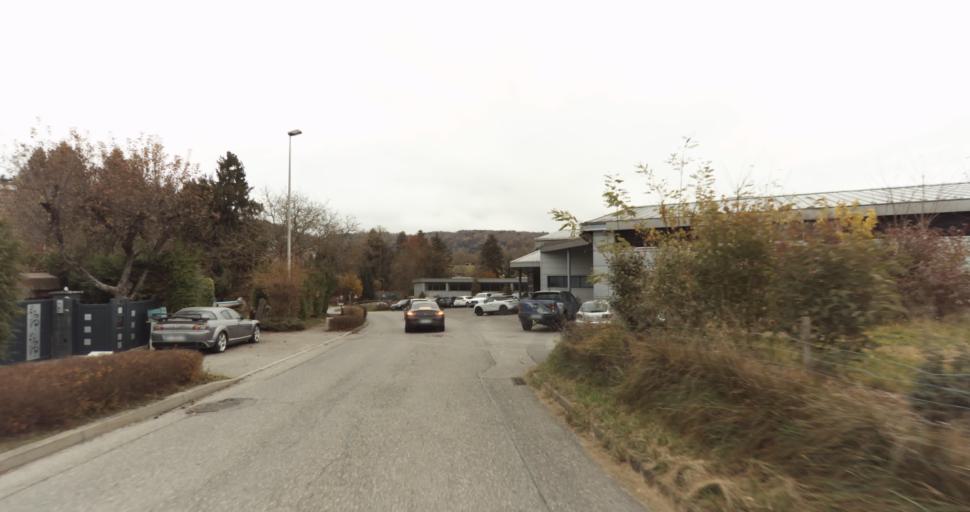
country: FR
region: Rhone-Alpes
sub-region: Departement de la Haute-Savoie
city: Metz-Tessy
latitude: 45.9483
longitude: 6.1069
